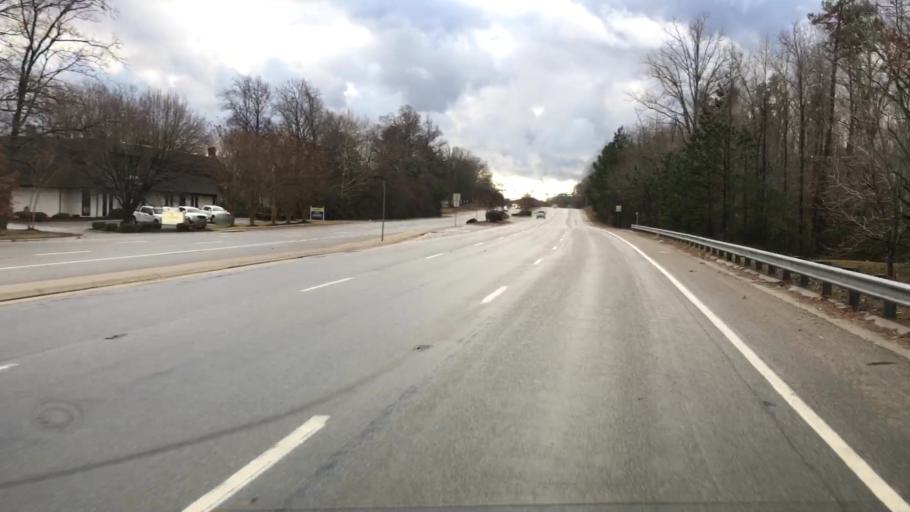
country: US
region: Virginia
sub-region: Chesterfield County
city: Bon Air
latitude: 37.5023
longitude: -77.6103
